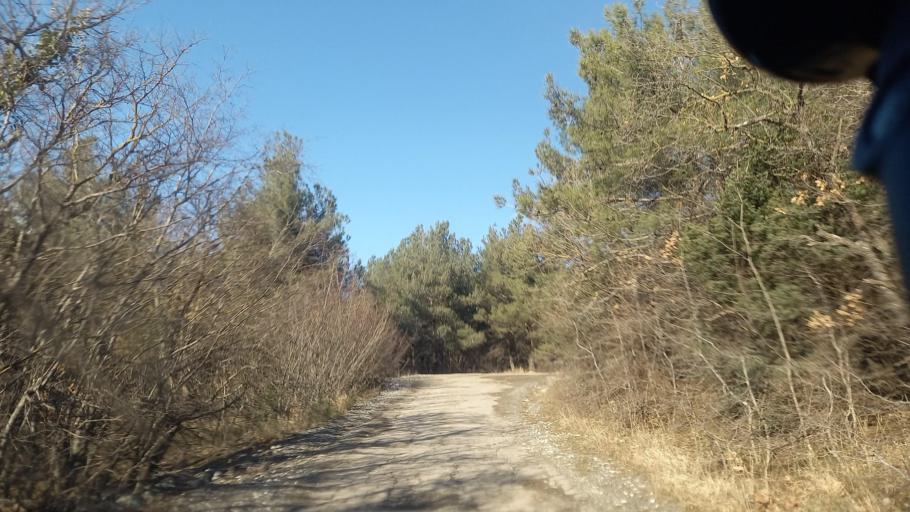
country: RU
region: Krasnodarskiy
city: Kabardinka
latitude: 44.6294
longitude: 37.9183
